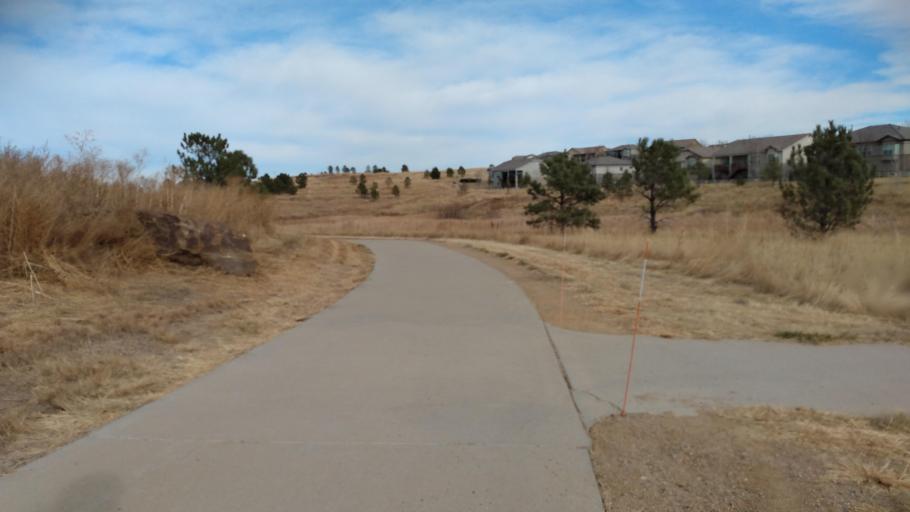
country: US
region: Colorado
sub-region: Boulder County
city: Lafayette
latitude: 39.9955
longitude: -105.0520
